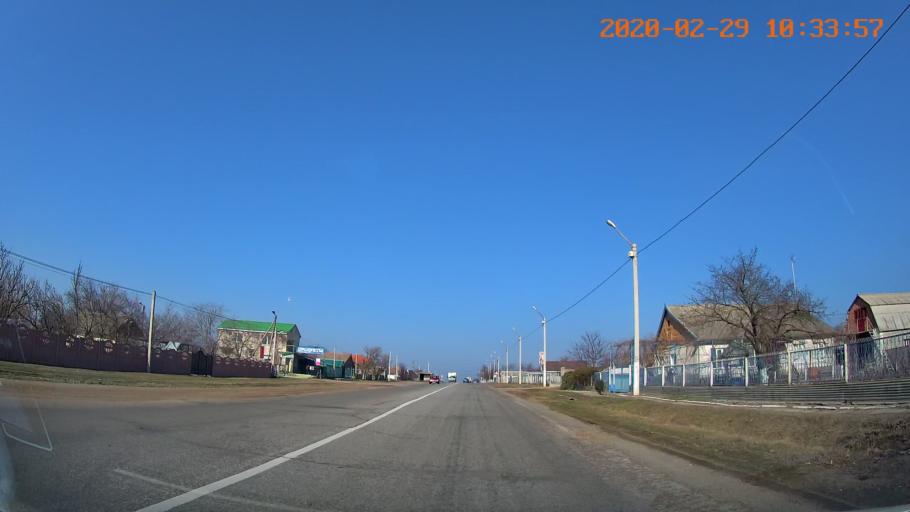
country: MD
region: Anenii Noi
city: Varnita
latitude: 46.9737
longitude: 29.5390
